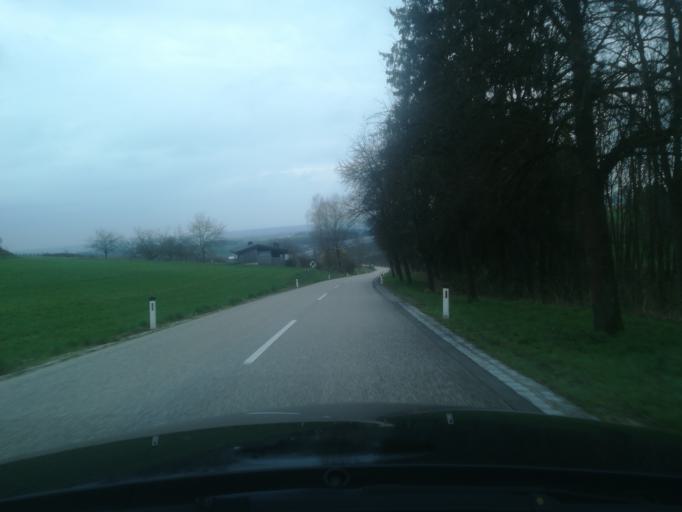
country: AT
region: Upper Austria
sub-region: Wels-Land
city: Buchkirchen
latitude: 48.2441
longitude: 14.0539
